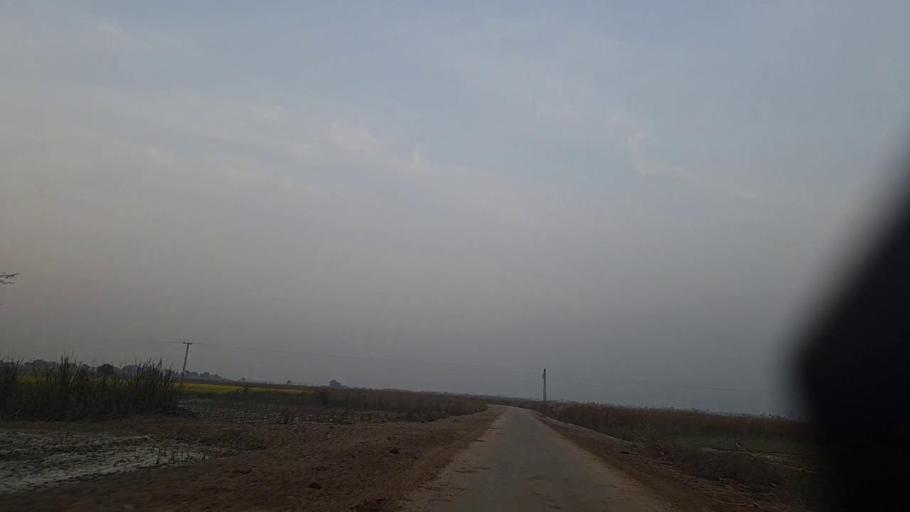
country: PK
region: Sindh
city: Sakrand
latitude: 26.0967
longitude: 68.3406
